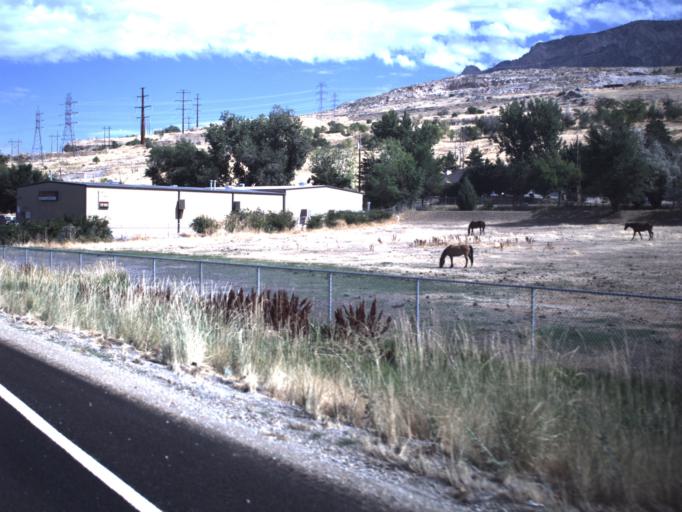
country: US
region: Utah
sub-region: Box Elder County
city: South Willard
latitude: 41.3319
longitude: -112.0246
